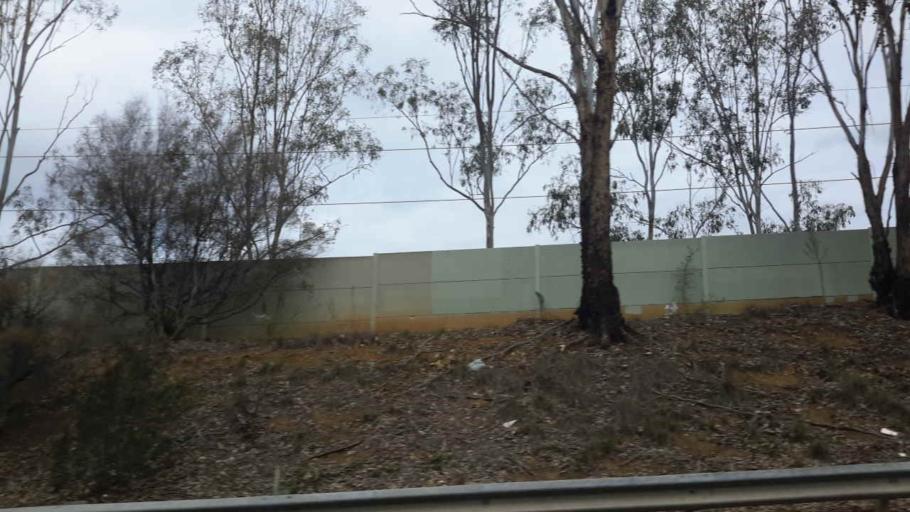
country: AU
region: New South Wales
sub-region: Camden
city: Narellan Vale
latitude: -34.0443
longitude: 150.7446
